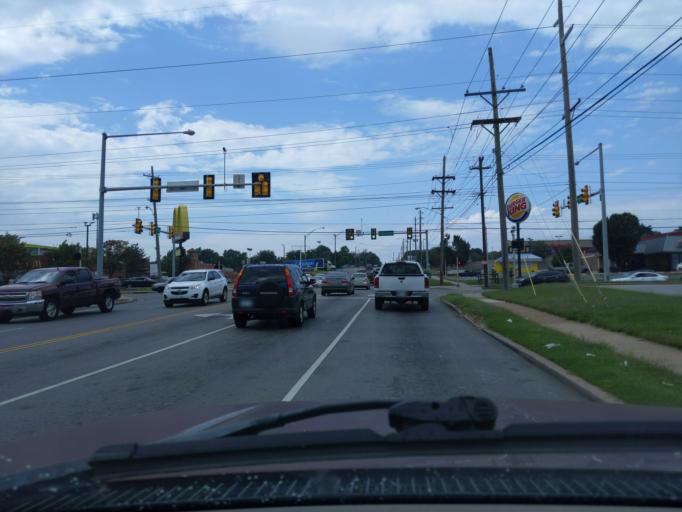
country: US
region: Oklahoma
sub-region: Tulsa County
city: Tulsa
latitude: 36.1335
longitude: -95.9041
